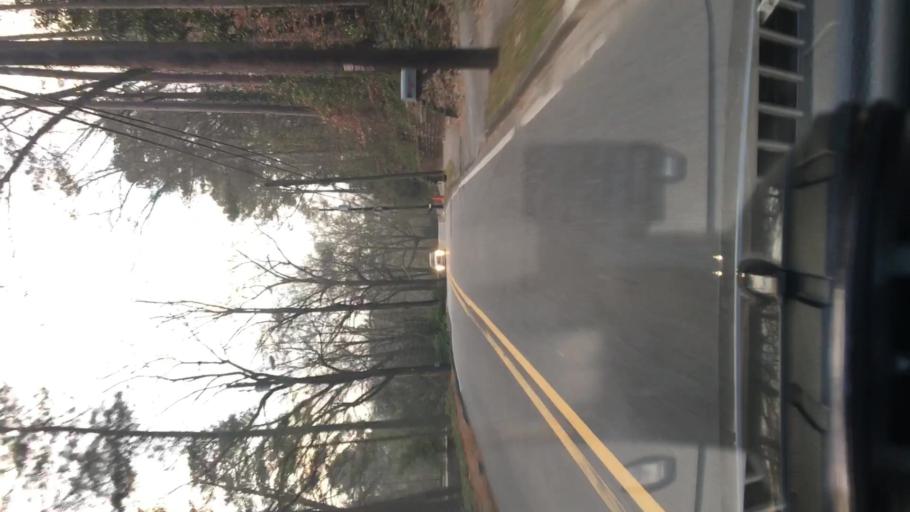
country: US
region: Georgia
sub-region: DeKalb County
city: North Atlanta
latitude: 33.8885
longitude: -84.3604
